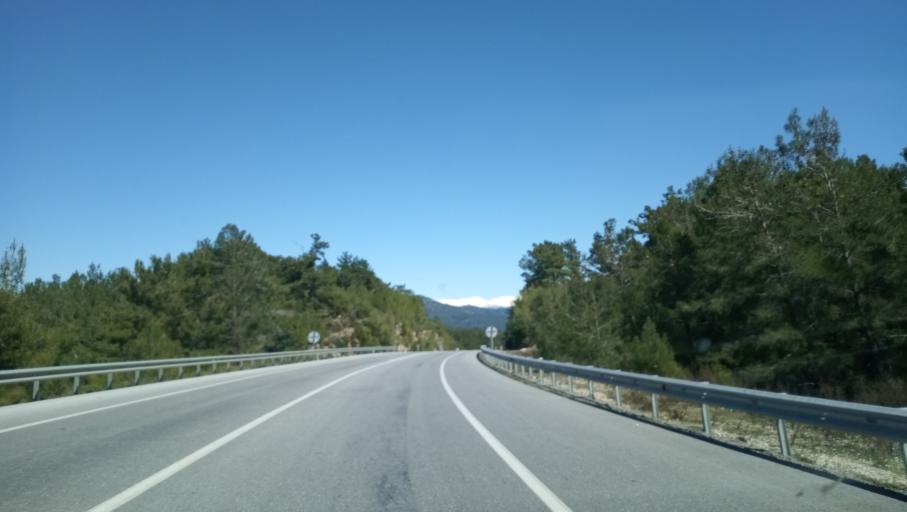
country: TR
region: Antalya
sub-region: Alanya
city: Okurcalar
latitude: 36.7716
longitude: 31.6759
